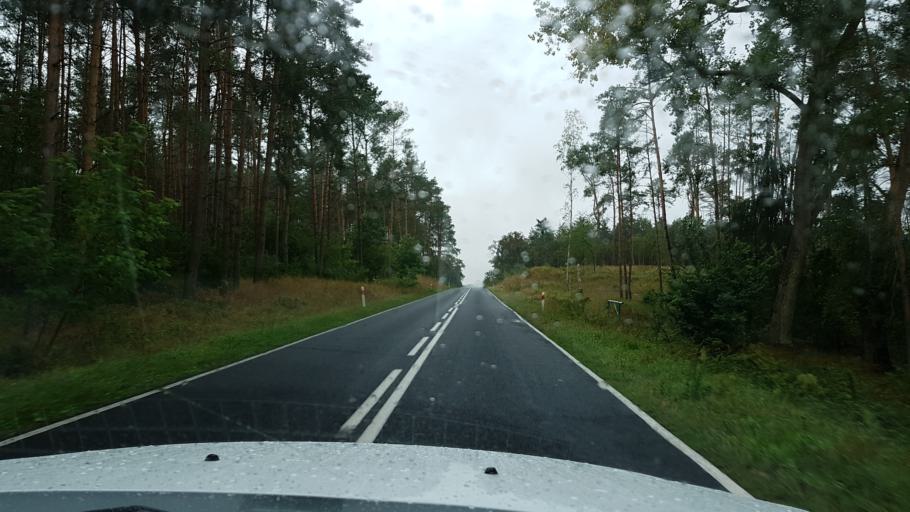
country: DE
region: Brandenburg
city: Schwedt (Oder)
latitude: 53.0397
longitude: 14.3298
